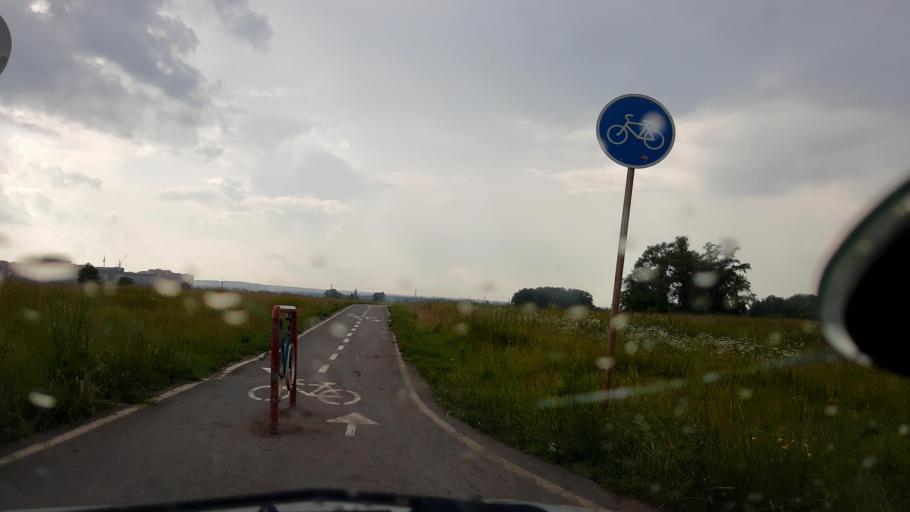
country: RU
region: Bashkortostan
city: Mikhaylovka
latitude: 54.7120
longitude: 55.8683
